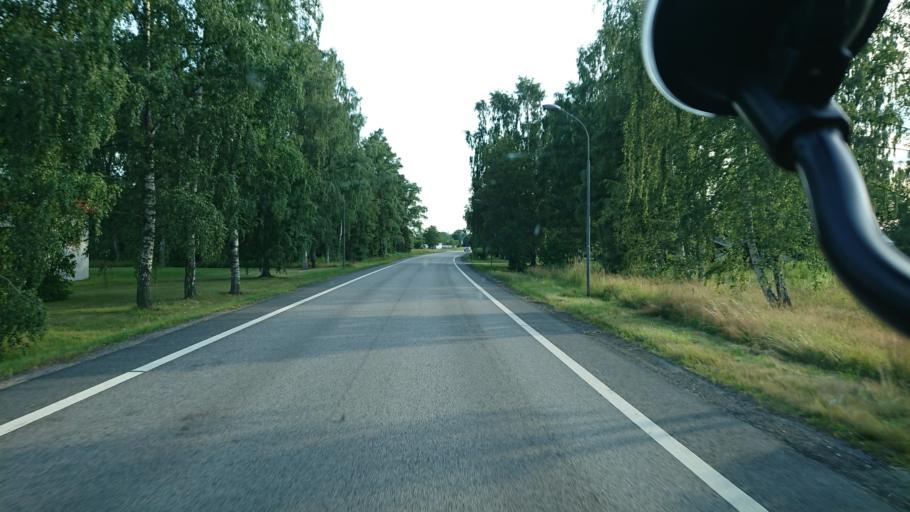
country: SE
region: Kronoberg
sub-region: Vaxjo Kommun
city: Rottne
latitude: 57.0293
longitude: 14.8940
